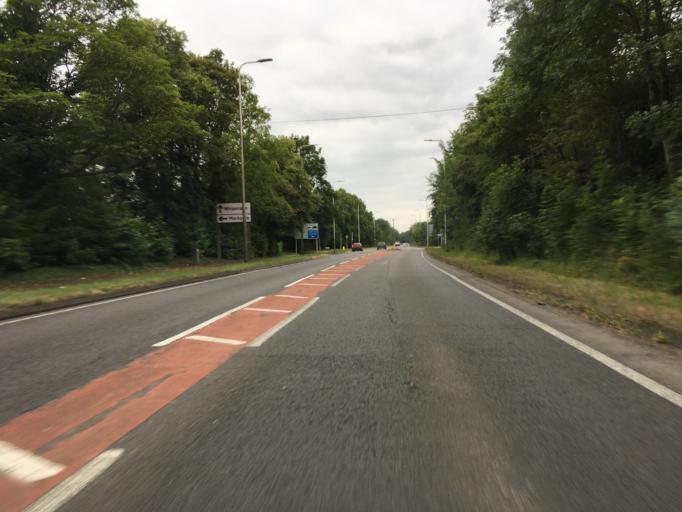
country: GB
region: England
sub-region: Hertfordshire
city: Markyate
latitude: 51.8311
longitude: -0.4497
